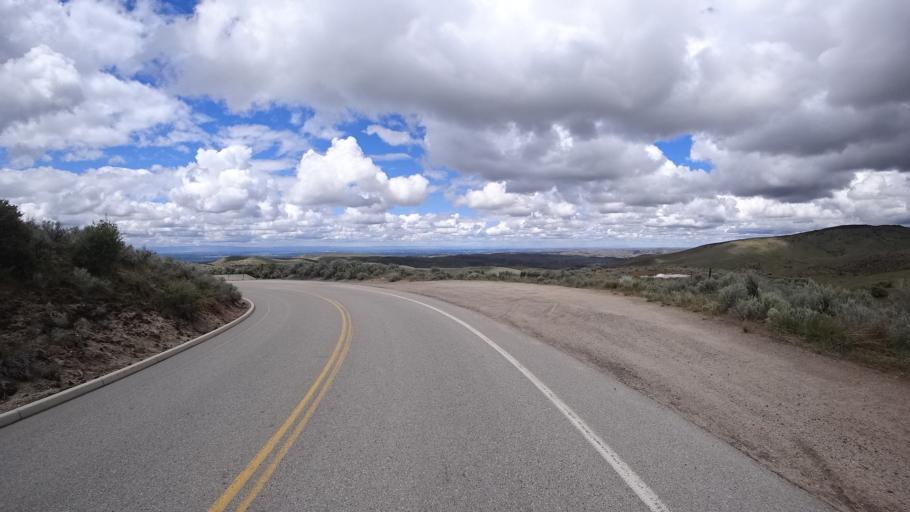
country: US
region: Idaho
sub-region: Ada County
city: Boise
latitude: 43.6950
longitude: -116.1783
